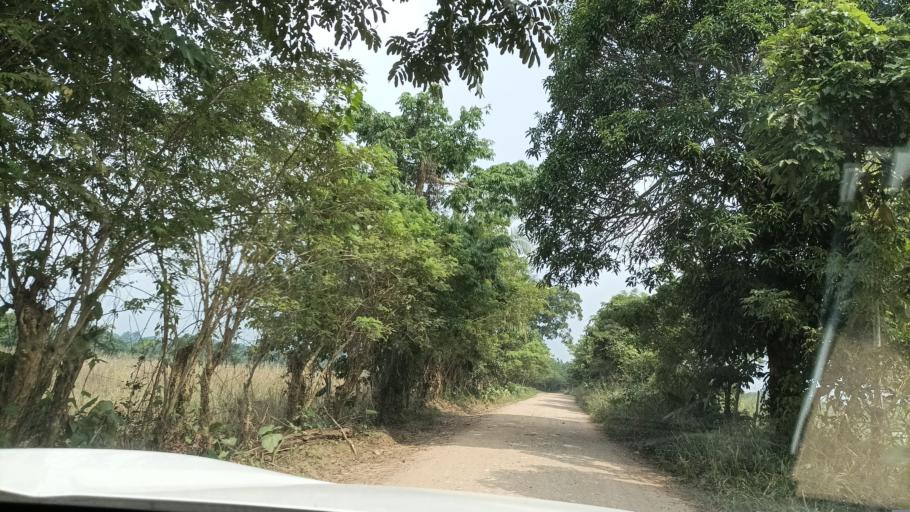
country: MX
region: Veracruz
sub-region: Moloacan
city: Cuichapa
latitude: 17.5825
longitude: -94.2197
